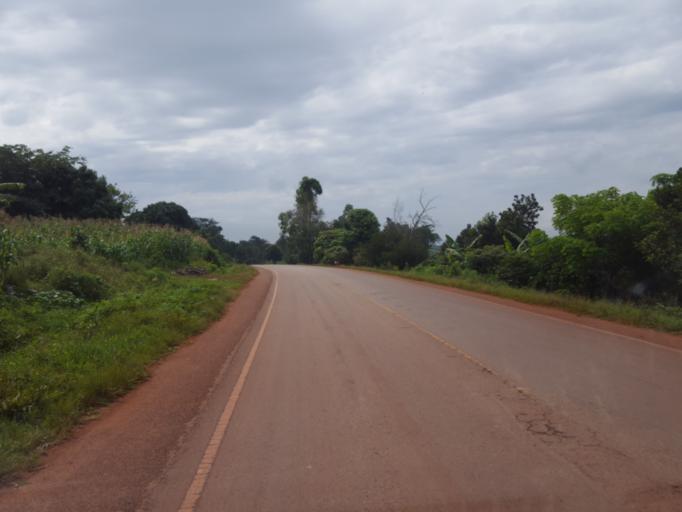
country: UG
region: Central Region
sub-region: Mityana District
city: Mityana
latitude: 0.6379
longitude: 32.1025
